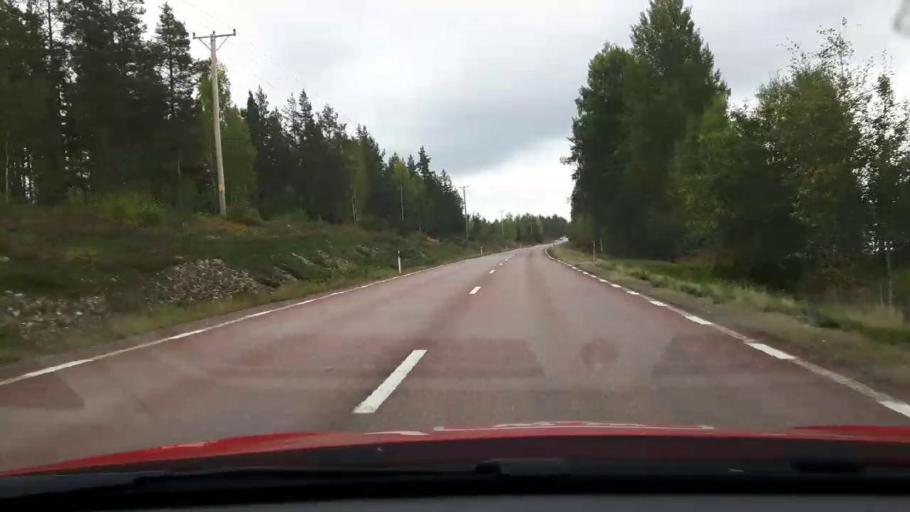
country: SE
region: Gaevleborg
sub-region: Soderhamns Kommun
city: Soderhamn
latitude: 61.1306
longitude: 16.9250
